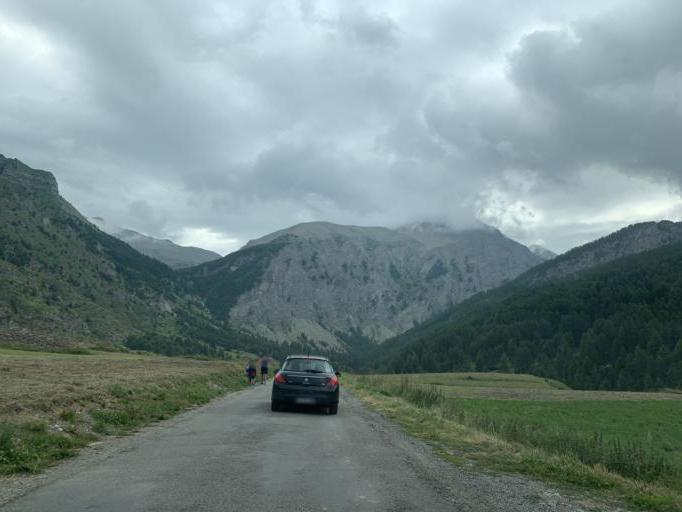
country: FR
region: Provence-Alpes-Cote d'Azur
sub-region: Departement des Hautes-Alpes
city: Guillestre
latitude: 44.5476
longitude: 6.6261
